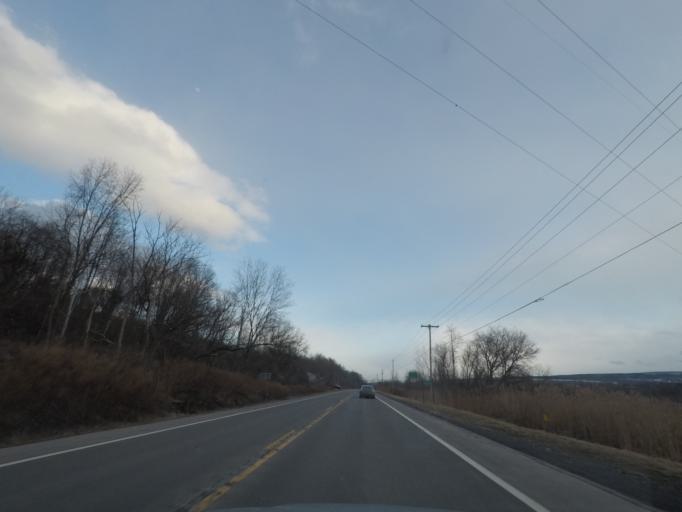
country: US
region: New York
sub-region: Herkimer County
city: Frankfort
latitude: 43.0347
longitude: -75.0512
